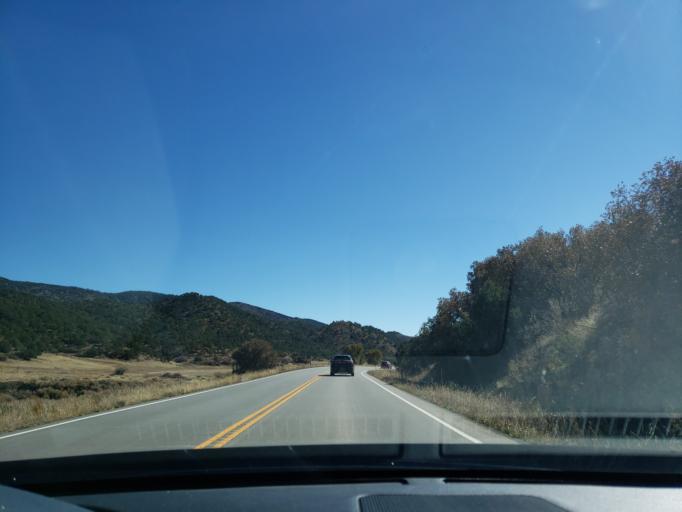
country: US
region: Colorado
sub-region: Fremont County
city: Canon City
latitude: 38.6028
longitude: -105.4321
